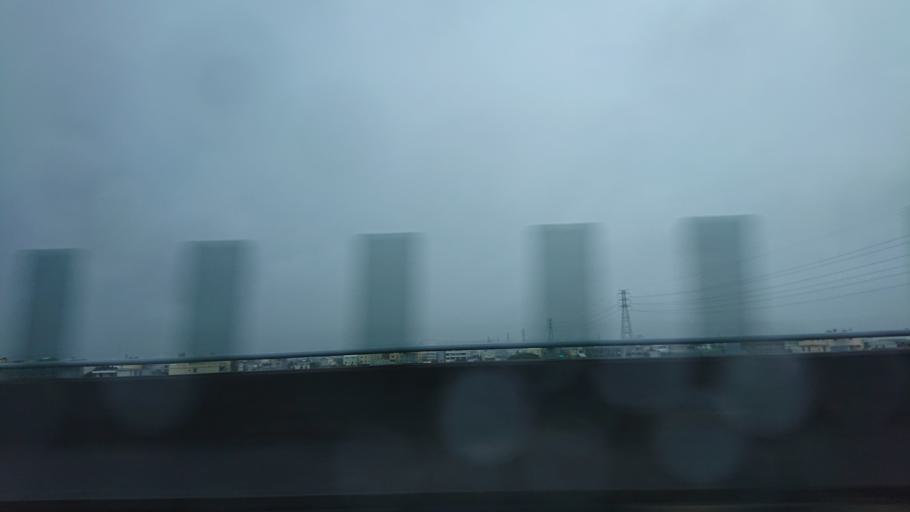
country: TW
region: Taiwan
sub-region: Changhua
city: Chang-hua
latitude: 24.2378
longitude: 120.5310
